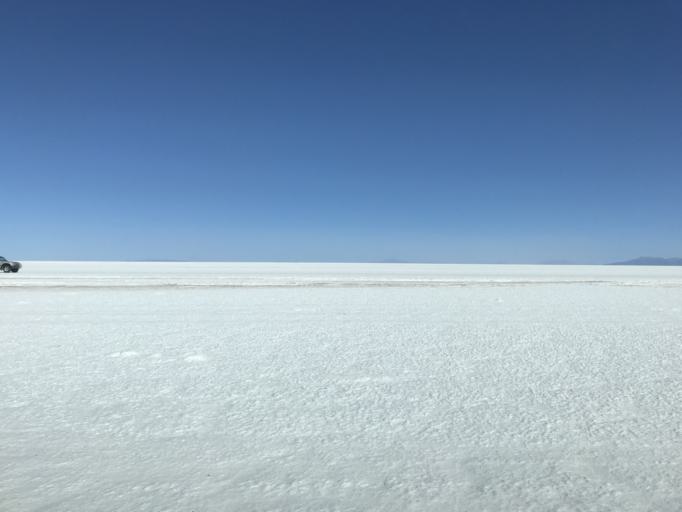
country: BO
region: Potosi
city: Colchani
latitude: -20.3084
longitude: -67.2920
